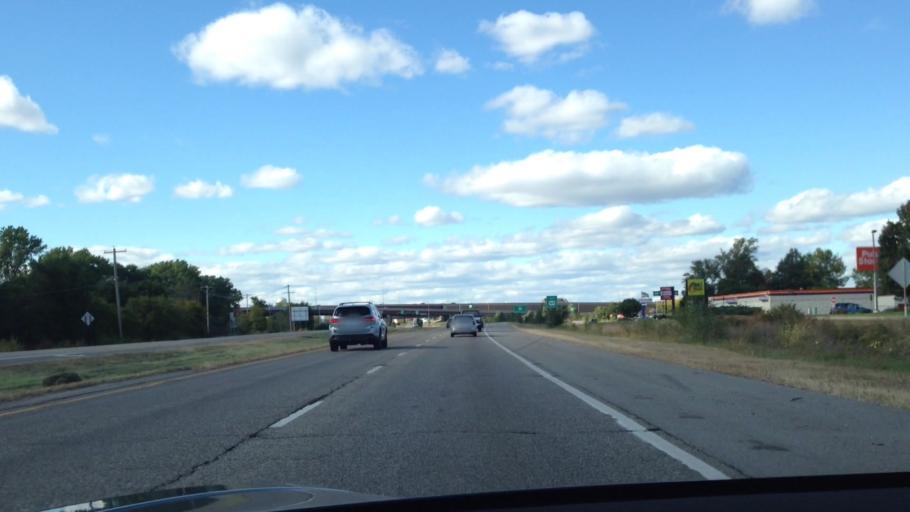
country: US
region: Minnesota
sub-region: Hennepin County
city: Osseo
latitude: 45.1016
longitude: -93.3895
